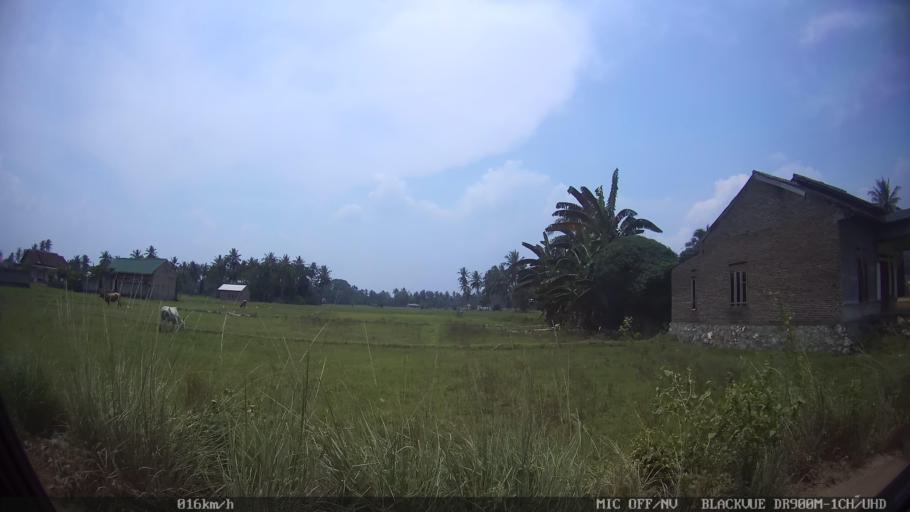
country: ID
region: Lampung
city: Natar
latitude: -5.3141
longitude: 105.2346
